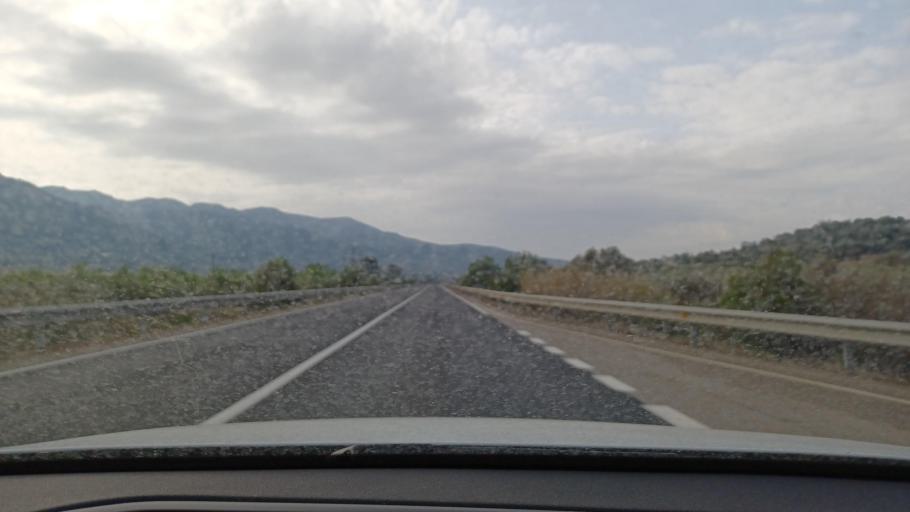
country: ES
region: Catalonia
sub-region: Provincia de Tarragona
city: Santa Barbara
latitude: 40.6629
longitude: 0.5075
